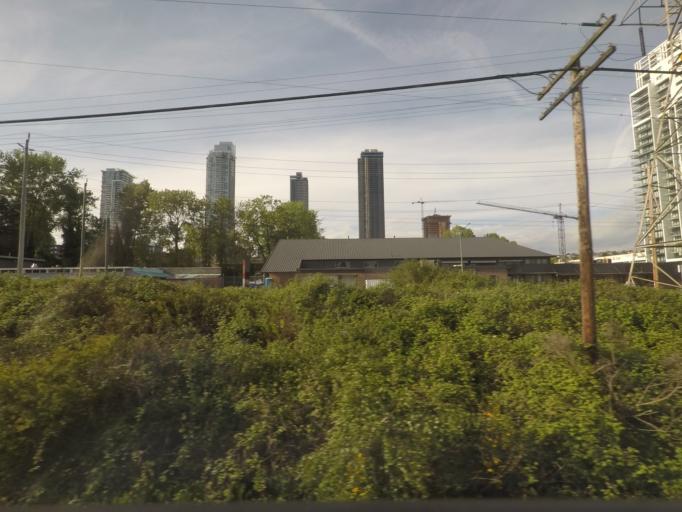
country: CA
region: British Columbia
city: Burnaby
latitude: 49.2621
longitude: -123.0018
